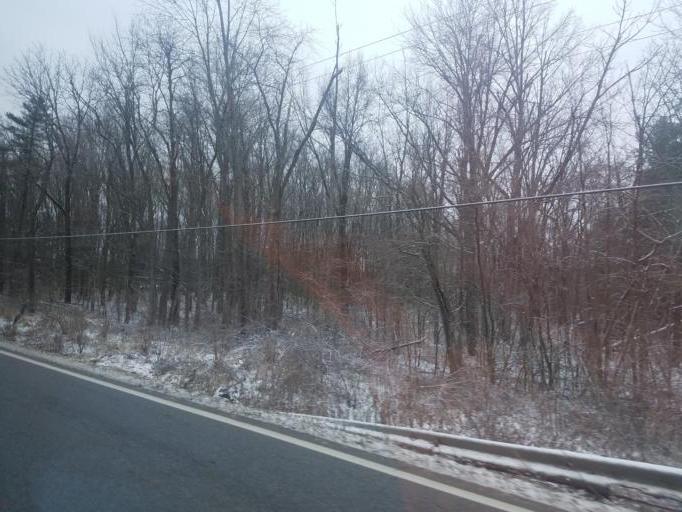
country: US
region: Ohio
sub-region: Licking County
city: Johnstown
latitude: 40.1968
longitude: -82.7668
